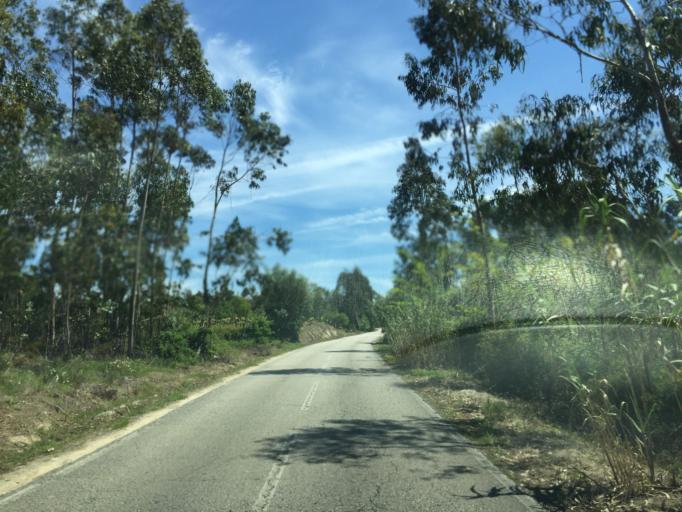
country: PT
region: Leiria
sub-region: Pombal
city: Lourical
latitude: 40.0658
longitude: -8.7210
